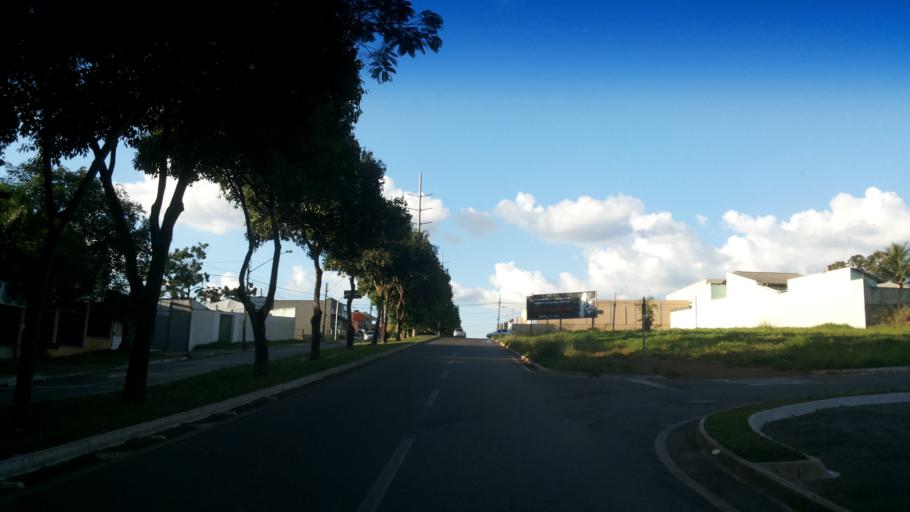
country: BR
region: Goias
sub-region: Goiania
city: Goiania
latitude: -16.7383
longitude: -49.3122
